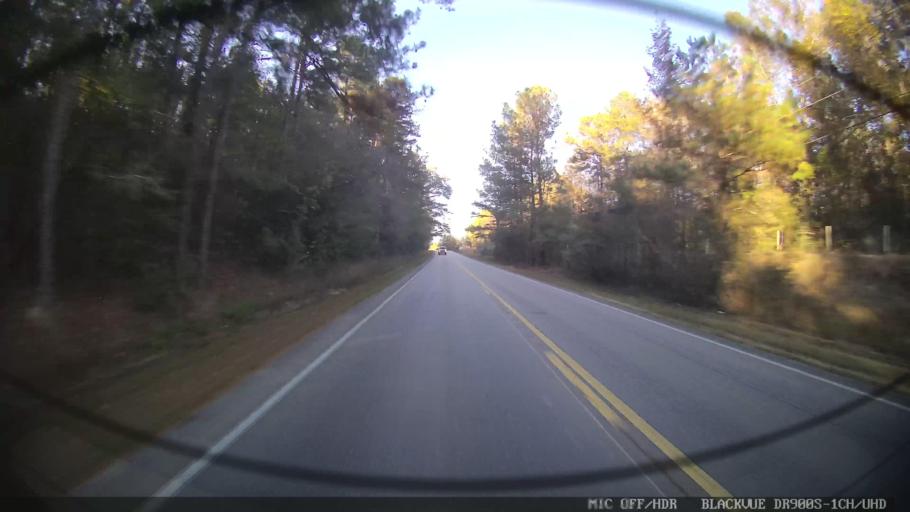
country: US
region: Mississippi
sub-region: Lamar County
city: Purvis
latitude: 31.0763
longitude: -89.4192
